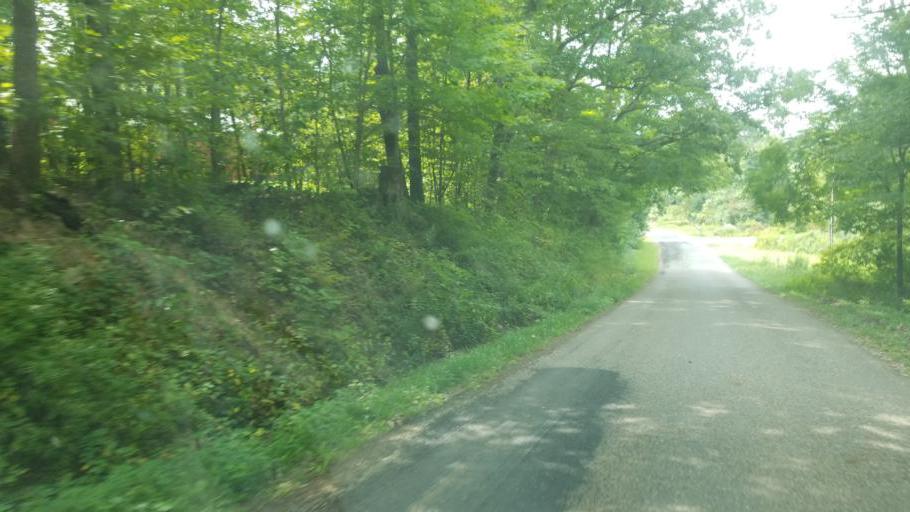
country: US
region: Ohio
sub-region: Knox County
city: Danville
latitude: 40.4801
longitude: -82.3353
